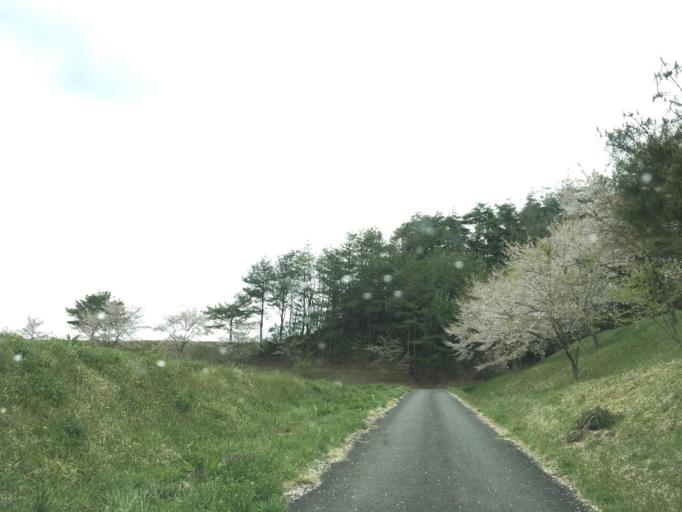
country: JP
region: Iwate
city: Ichinoseki
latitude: 38.8538
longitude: 141.3264
